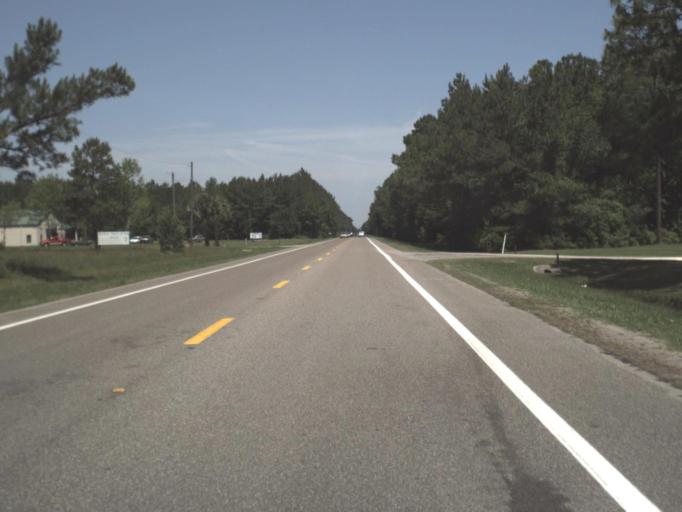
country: US
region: Florida
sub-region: Suwannee County
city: Wellborn
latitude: 30.2104
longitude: -82.8111
